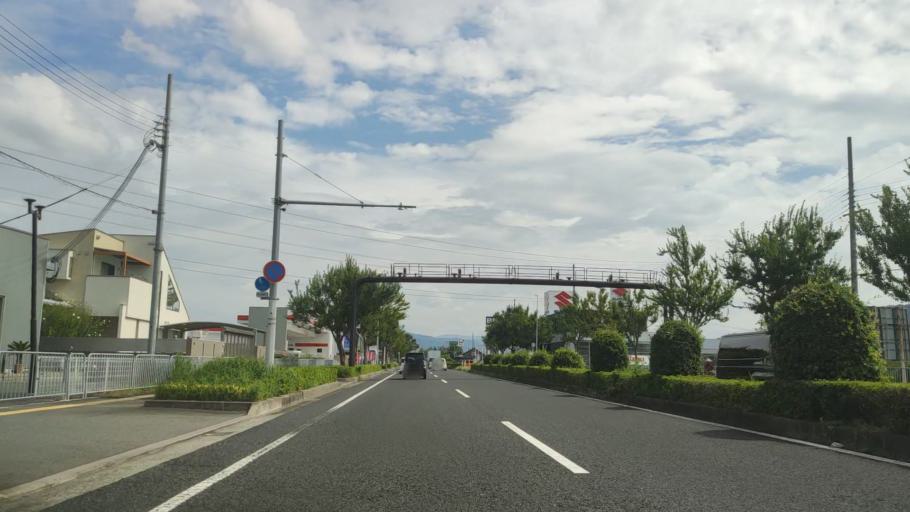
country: JP
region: Wakayama
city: Iwade
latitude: 34.2610
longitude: 135.2960
